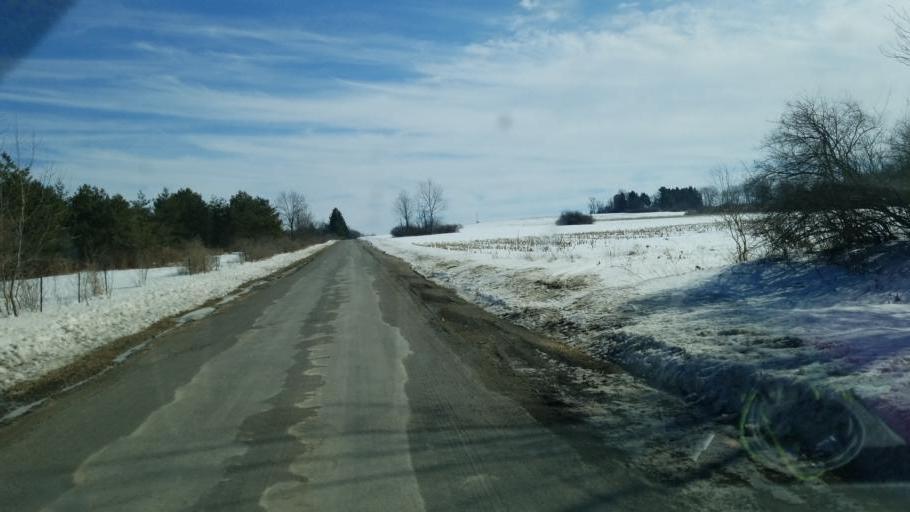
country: US
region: New York
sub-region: Allegany County
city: Andover
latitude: 42.1194
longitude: -77.7645
